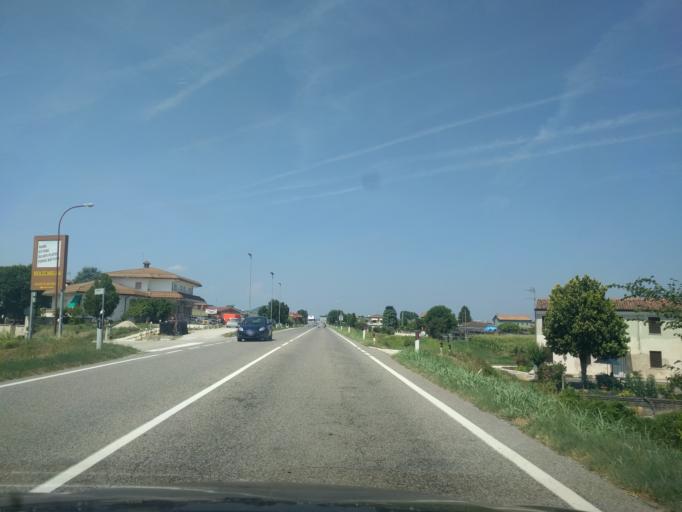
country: IT
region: Veneto
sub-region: Provincia di Padova
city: Solesino
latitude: 45.1712
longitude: 11.7564
